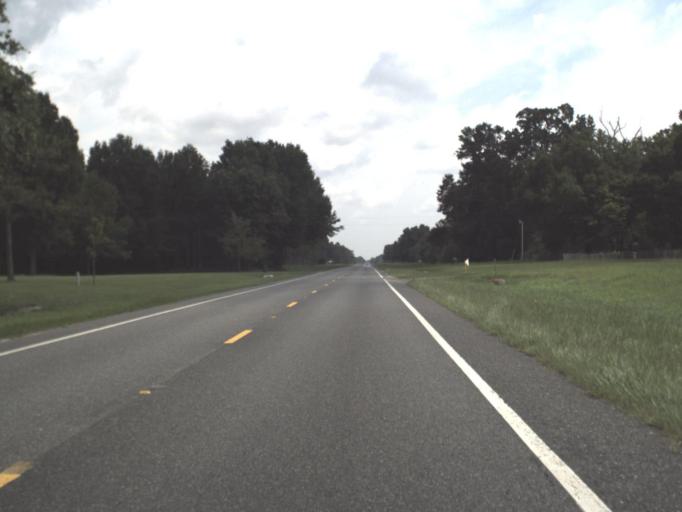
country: US
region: Florida
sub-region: Alachua County
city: High Springs
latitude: 29.8757
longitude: -82.6089
